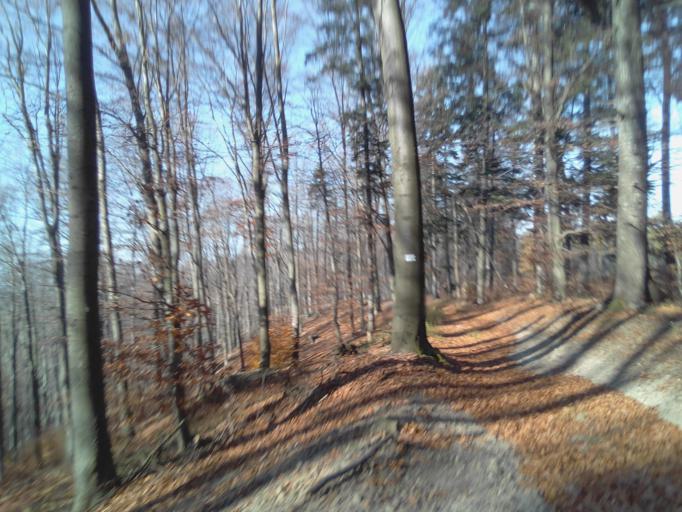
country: PL
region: Subcarpathian Voivodeship
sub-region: Powiat krosnienski
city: Leki
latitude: 49.8283
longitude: 21.6865
